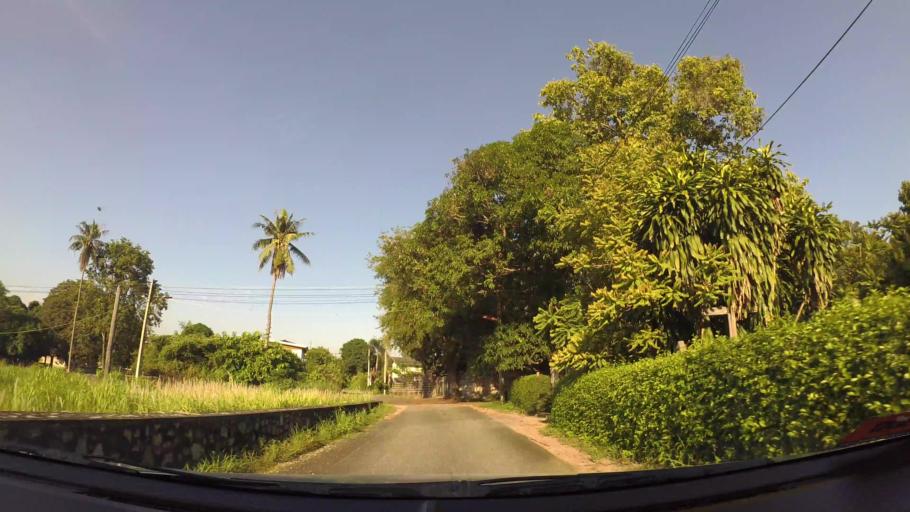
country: TH
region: Chon Buri
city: Si Racha
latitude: 13.1437
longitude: 100.9354
